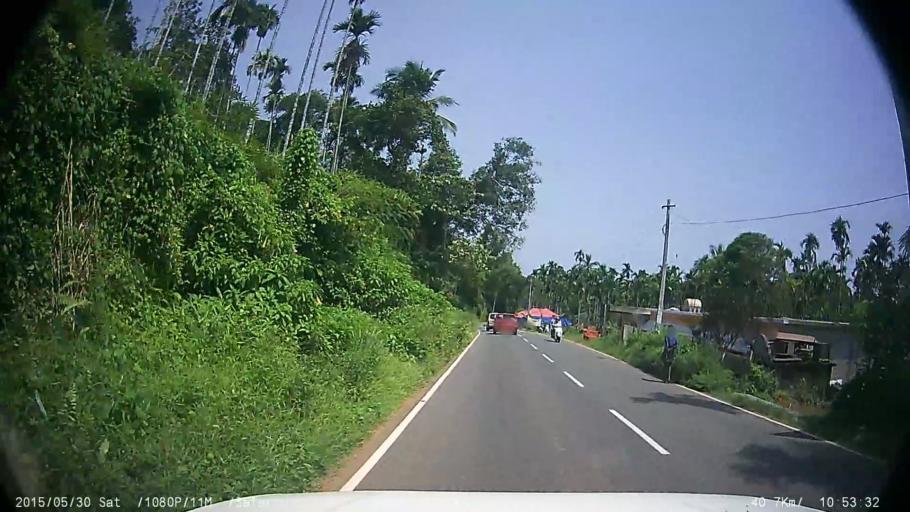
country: IN
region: Kerala
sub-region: Wayanad
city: Kalpetta
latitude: 11.6589
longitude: 76.0858
